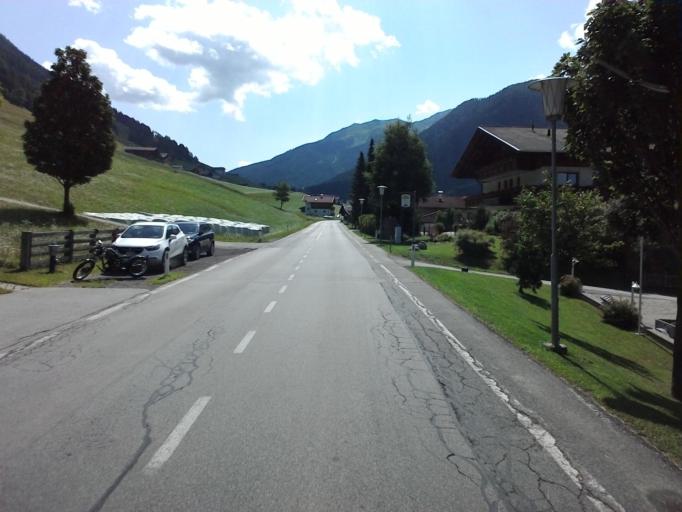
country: AT
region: Tyrol
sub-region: Politischer Bezirk Lienz
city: Kartitsch
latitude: 46.7315
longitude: 12.4872
